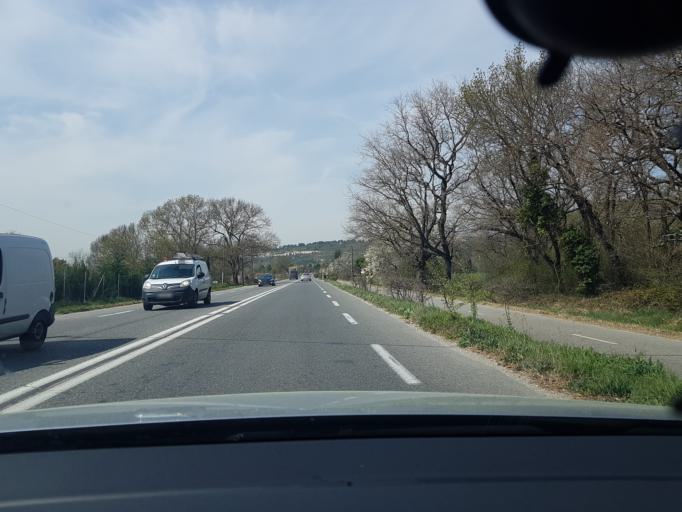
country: FR
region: Provence-Alpes-Cote d'Azur
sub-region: Departement des Bouches-du-Rhone
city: Chateauneuf-le-Rouge
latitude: 43.4735
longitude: 5.5770
